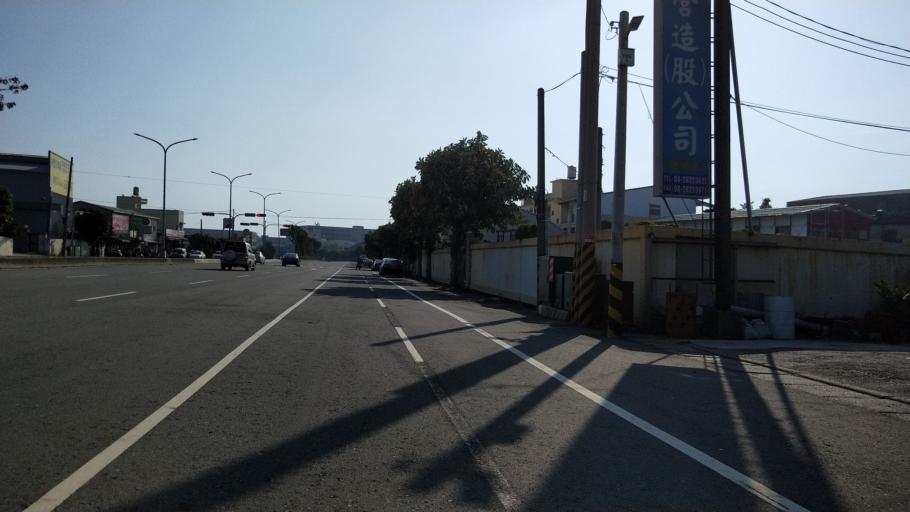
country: TW
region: Taiwan
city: Fengyuan
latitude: 24.2971
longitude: 120.5918
